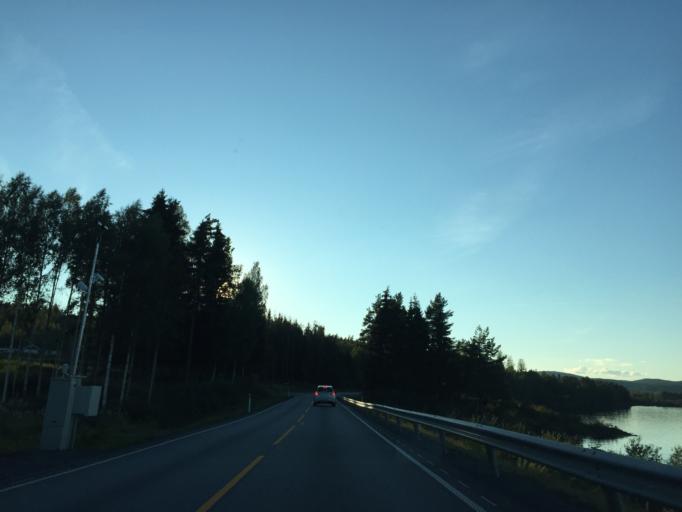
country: NO
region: Hedmark
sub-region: Nord-Odal
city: Sand
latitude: 60.3581
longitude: 11.5935
